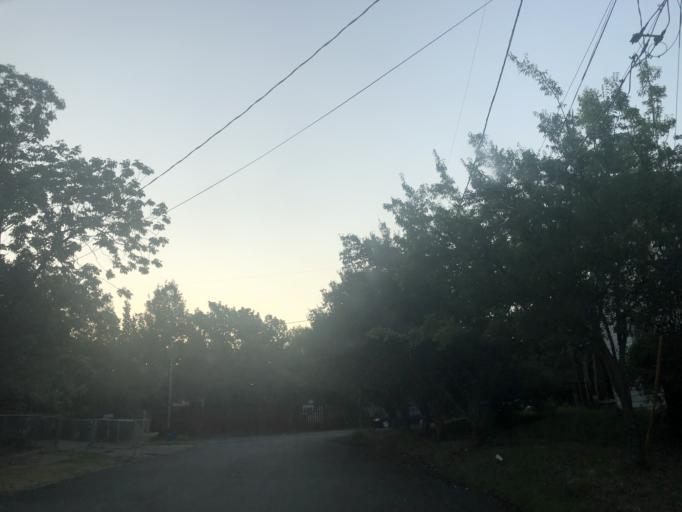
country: US
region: Texas
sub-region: Dallas County
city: Dallas
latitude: 32.7514
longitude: -96.8196
